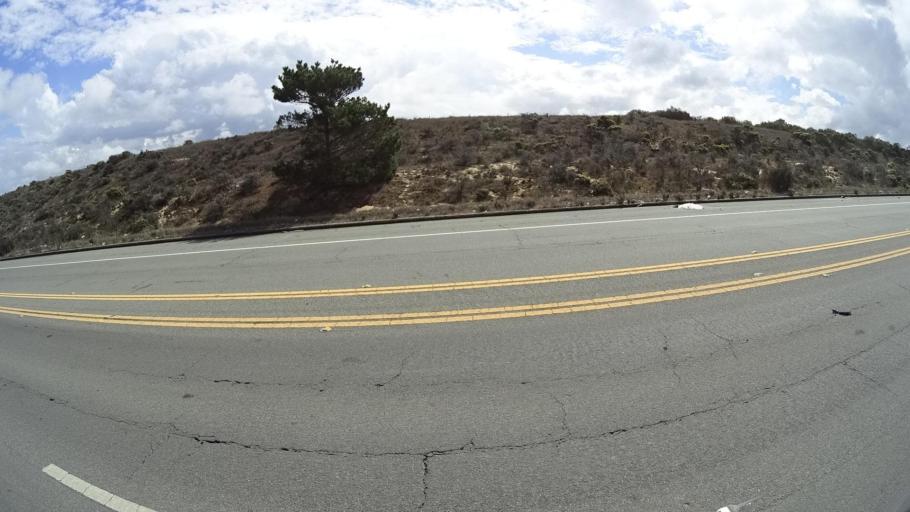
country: US
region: California
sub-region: Monterey County
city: Marina
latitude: 36.6725
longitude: -121.7616
